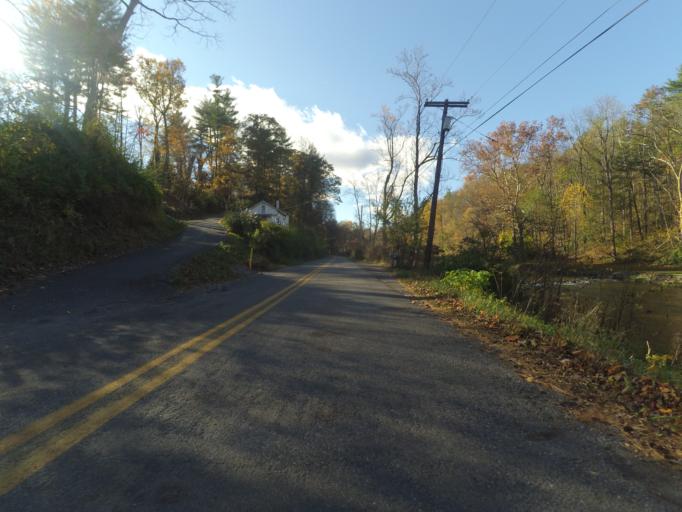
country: US
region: Pennsylvania
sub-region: Centre County
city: Bellefonte
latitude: 40.8831
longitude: -77.7870
